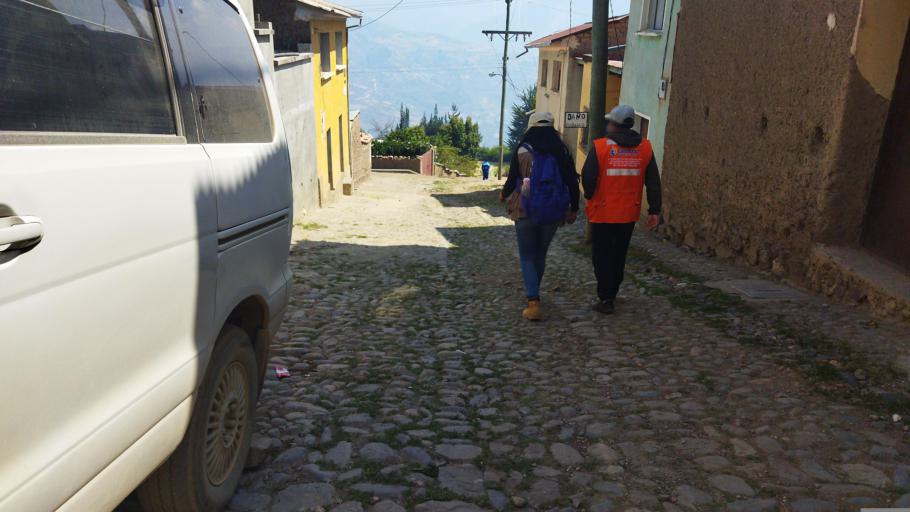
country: BO
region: La Paz
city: Quime
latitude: -16.9068
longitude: -67.1373
